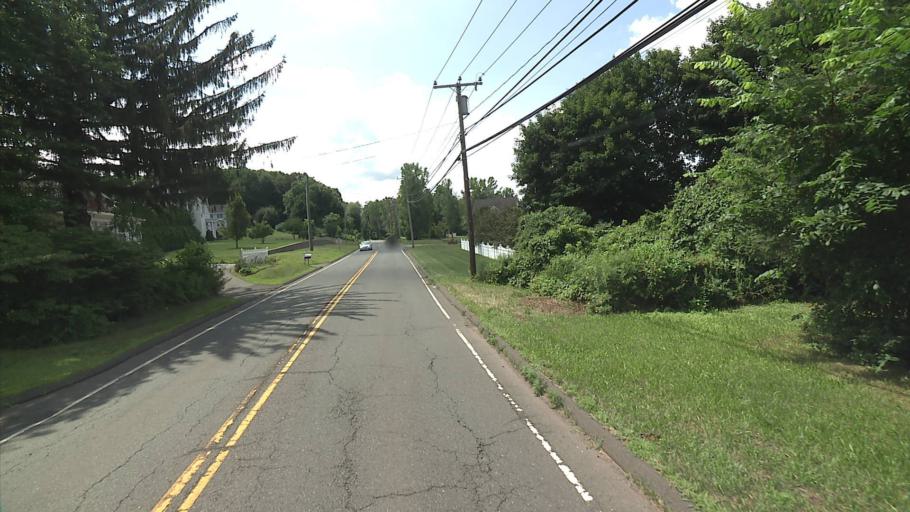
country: US
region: Connecticut
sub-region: Middlesex County
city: Cromwell
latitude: 41.6248
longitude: -72.6014
